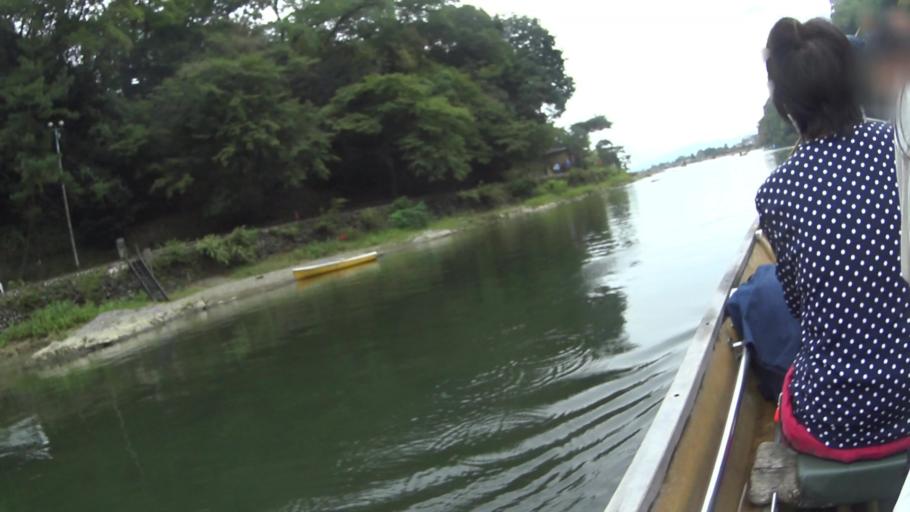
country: JP
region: Kyoto
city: Muko
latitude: 35.0136
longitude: 135.6712
